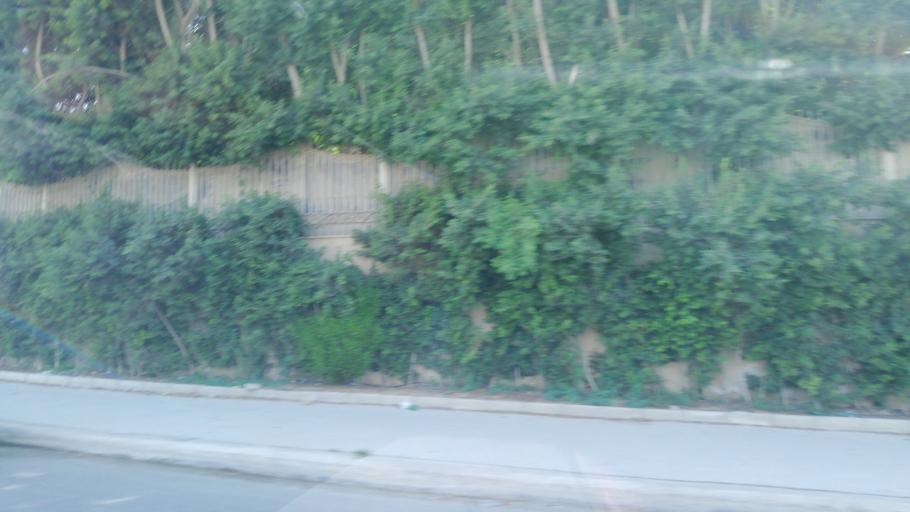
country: EG
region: Muhafazat al Qalyubiyah
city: Al Khankah
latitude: 30.0531
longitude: 31.4981
